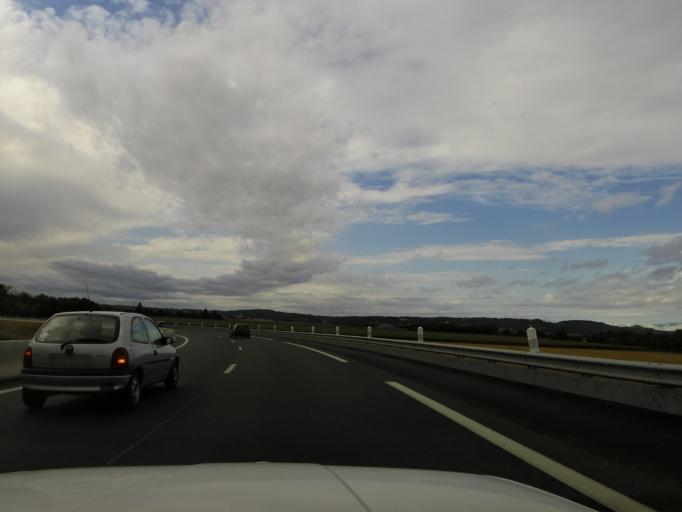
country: FR
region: Rhone-Alpes
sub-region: Departement du Rhone
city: Saint-Laurent-de-Mure
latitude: 45.6708
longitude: 5.0441
